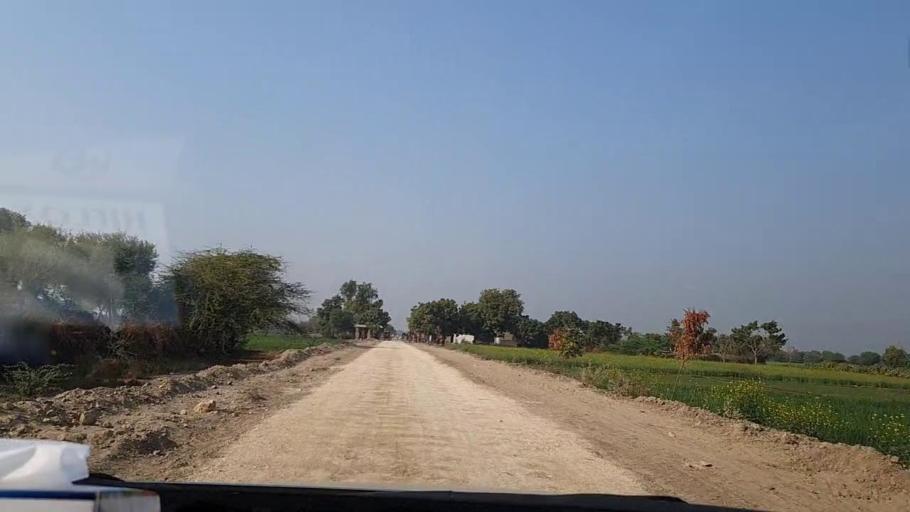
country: PK
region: Sindh
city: Tando Ghulam Ali
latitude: 25.1766
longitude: 68.8766
